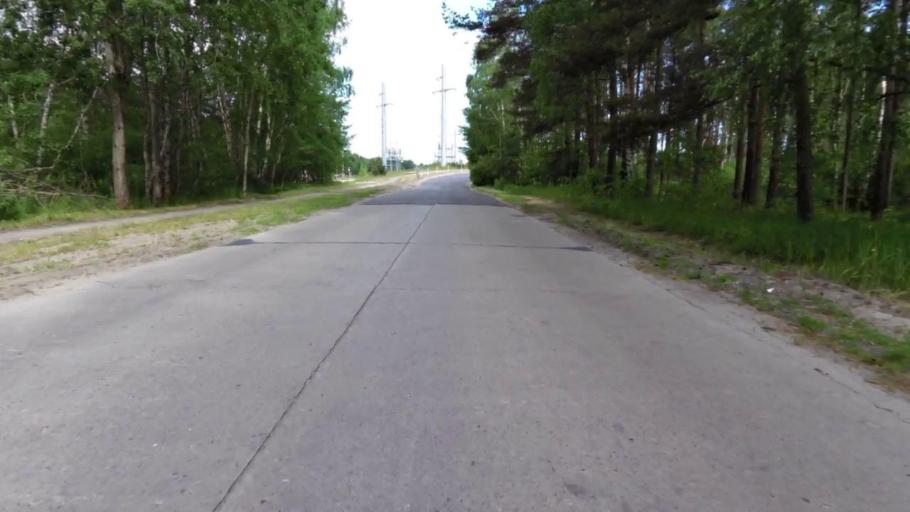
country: PL
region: West Pomeranian Voivodeship
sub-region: Swinoujscie
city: Swinoujscie
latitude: 53.9029
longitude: 14.2968
